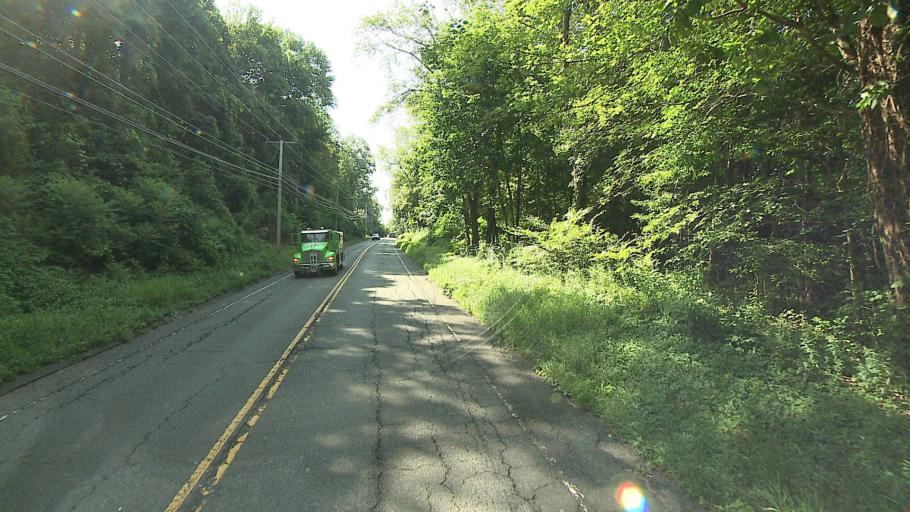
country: US
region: Connecticut
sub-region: Fairfield County
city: Danbury
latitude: 41.4558
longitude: -73.4768
